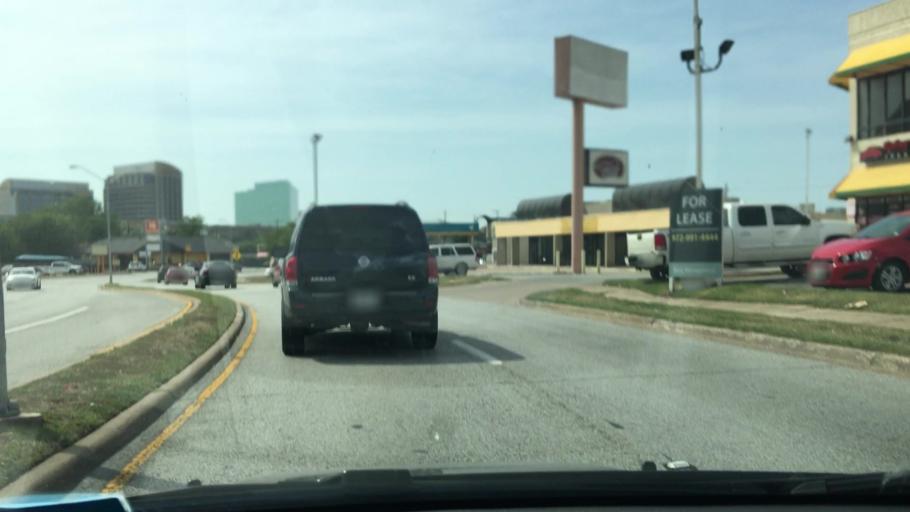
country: US
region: Texas
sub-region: Dallas County
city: Addison
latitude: 32.9315
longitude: -96.8117
